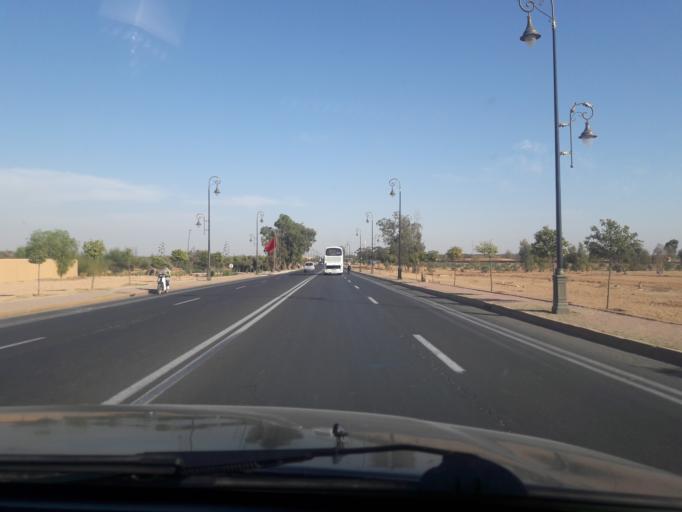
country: MA
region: Marrakech-Tensift-Al Haouz
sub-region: Marrakech
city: Marrakesh
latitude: 31.6480
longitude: -7.9360
